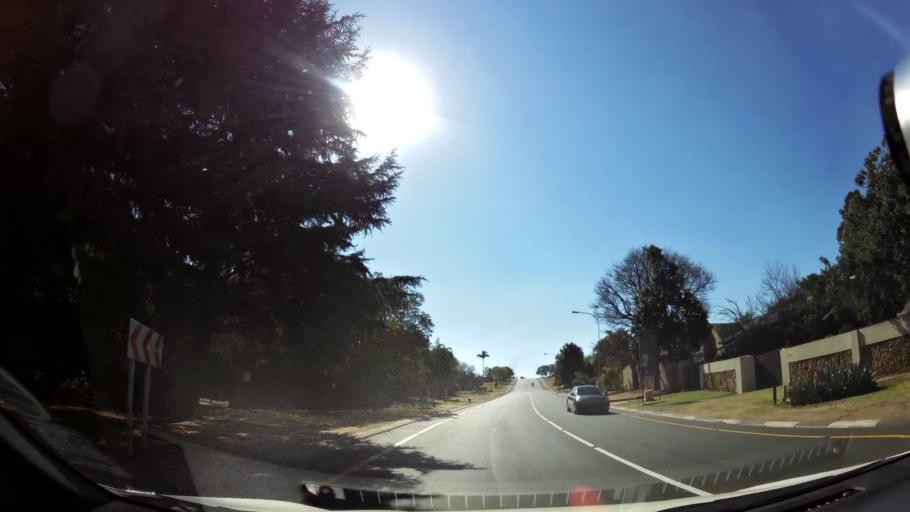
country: ZA
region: Gauteng
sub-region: City of Johannesburg Metropolitan Municipality
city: Johannesburg
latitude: -26.2641
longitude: 27.9951
